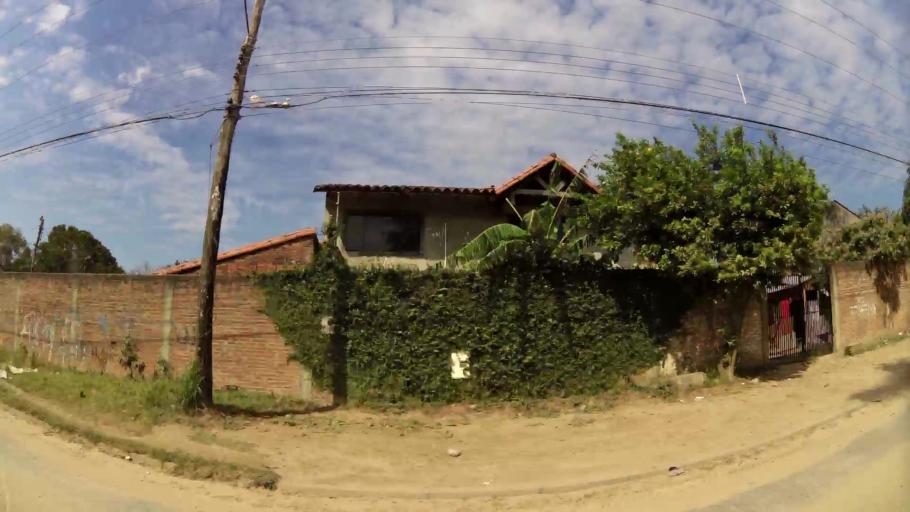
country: BO
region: Santa Cruz
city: Santa Cruz de la Sierra
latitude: -17.7265
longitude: -63.1791
